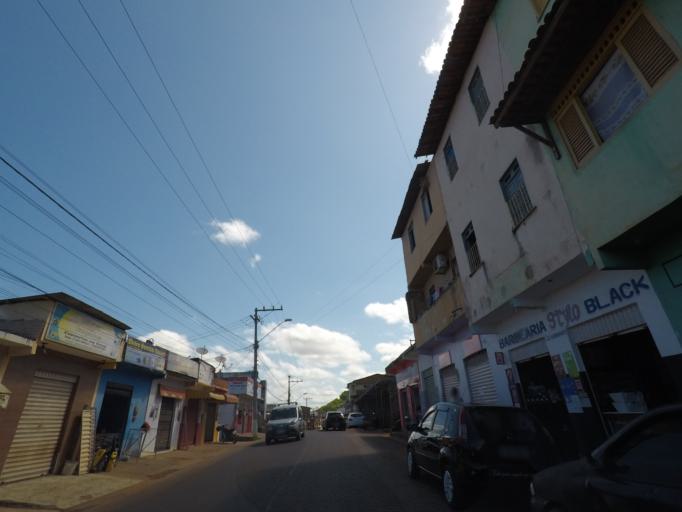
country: BR
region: Bahia
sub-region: Itubera
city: Itubera
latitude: -13.7387
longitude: -39.1493
